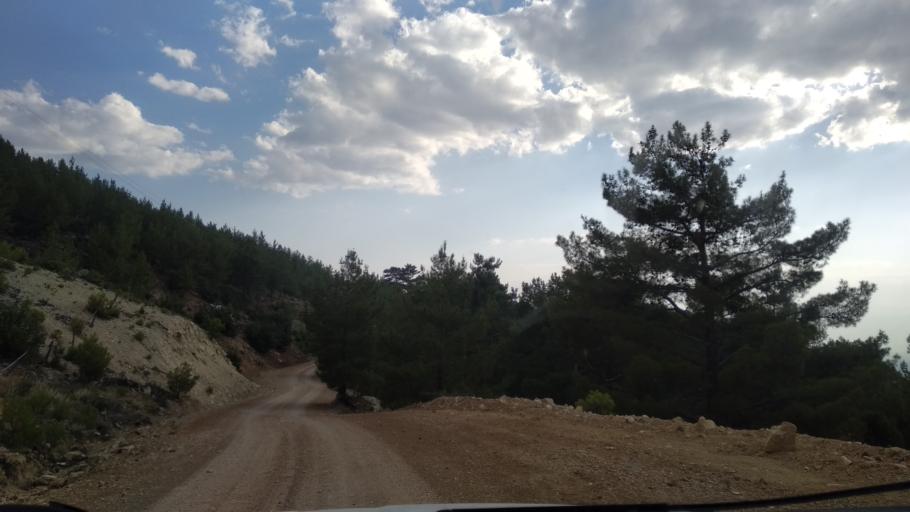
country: TR
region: Mersin
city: Sarikavak
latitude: 36.5960
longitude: 33.6858
